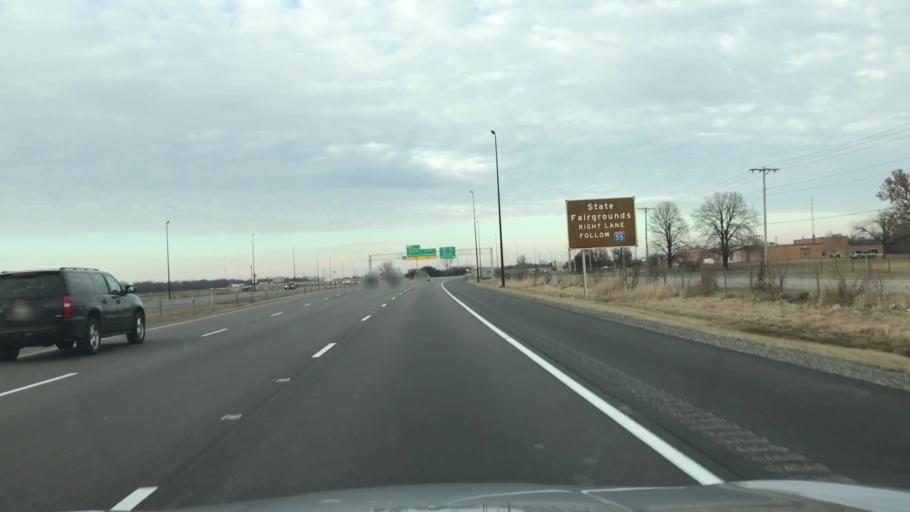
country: US
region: Illinois
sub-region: Sangamon County
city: Southern View
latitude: 39.7321
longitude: -89.6444
